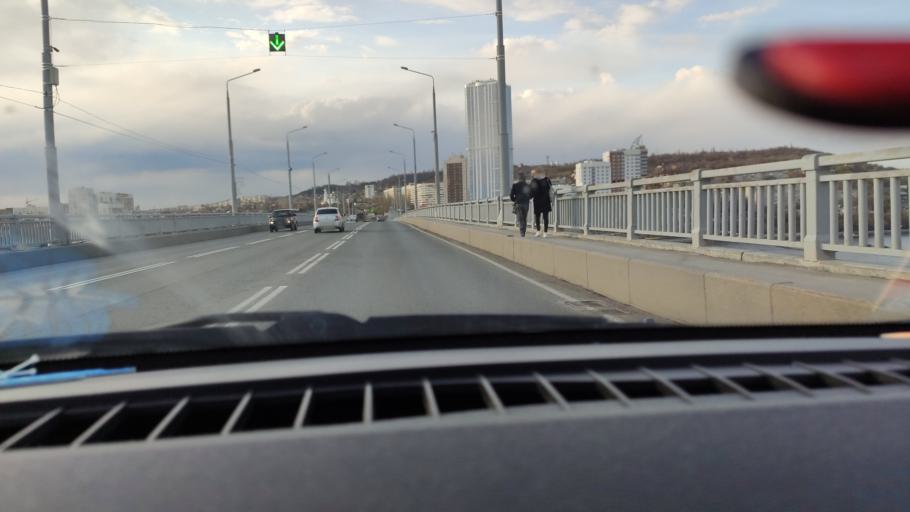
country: RU
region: Saratov
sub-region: Saratovskiy Rayon
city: Saratov
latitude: 51.5272
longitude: 46.0642
